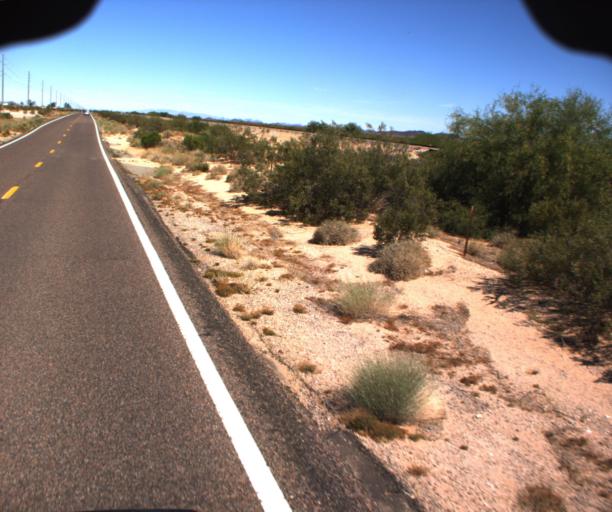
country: US
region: Arizona
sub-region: La Paz County
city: Salome
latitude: 33.8571
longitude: -113.9127
